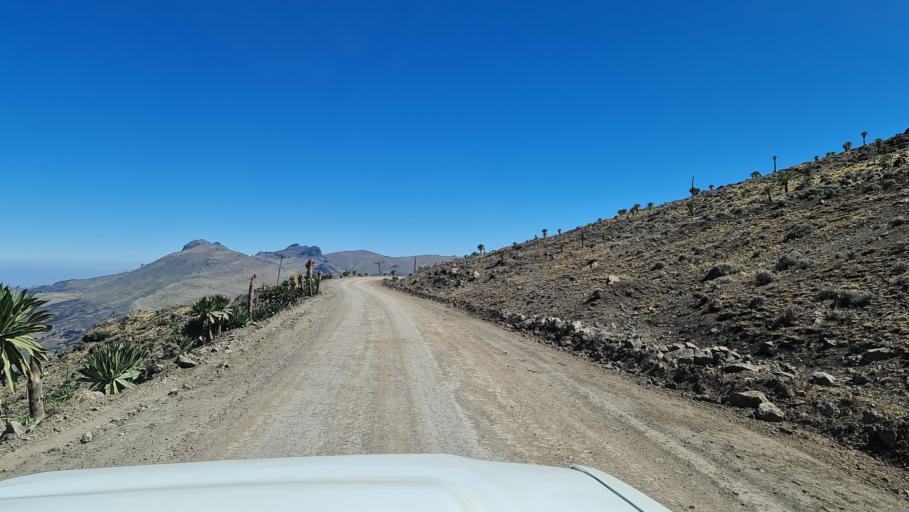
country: ET
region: Amhara
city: Debark'
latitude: 13.2512
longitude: 38.2110
